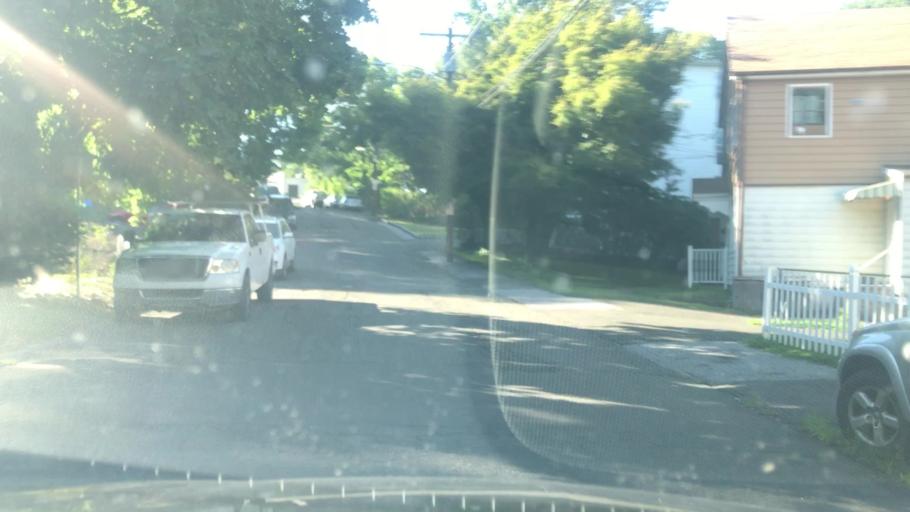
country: US
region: Connecticut
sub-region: Fairfield County
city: Greenwich
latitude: 41.0229
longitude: -73.6350
